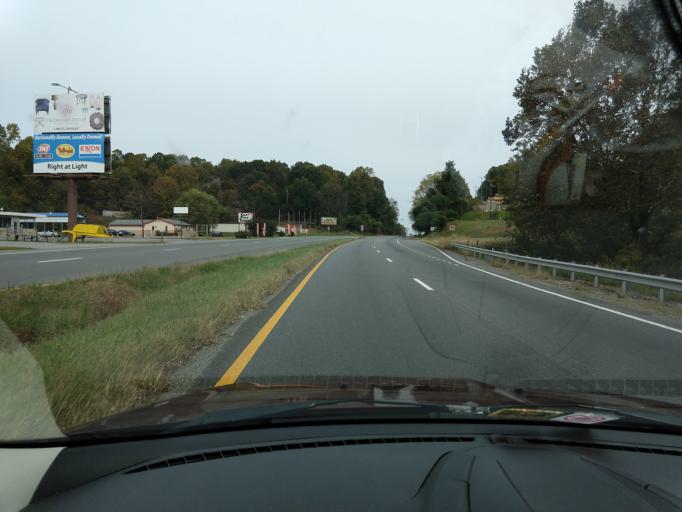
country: US
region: Virginia
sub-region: Franklin County
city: Rocky Mount
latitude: 37.0323
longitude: -79.8788
